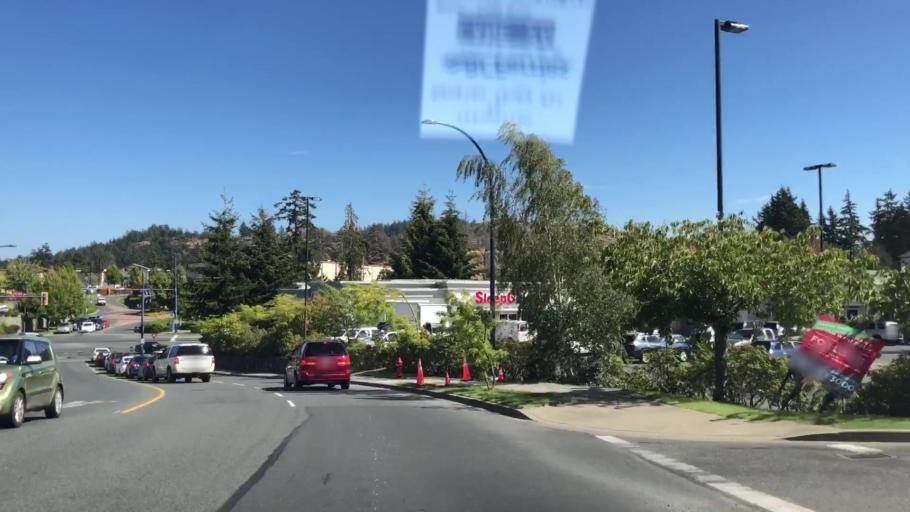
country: CA
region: British Columbia
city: Langford
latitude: 48.4601
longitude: -123.4990
